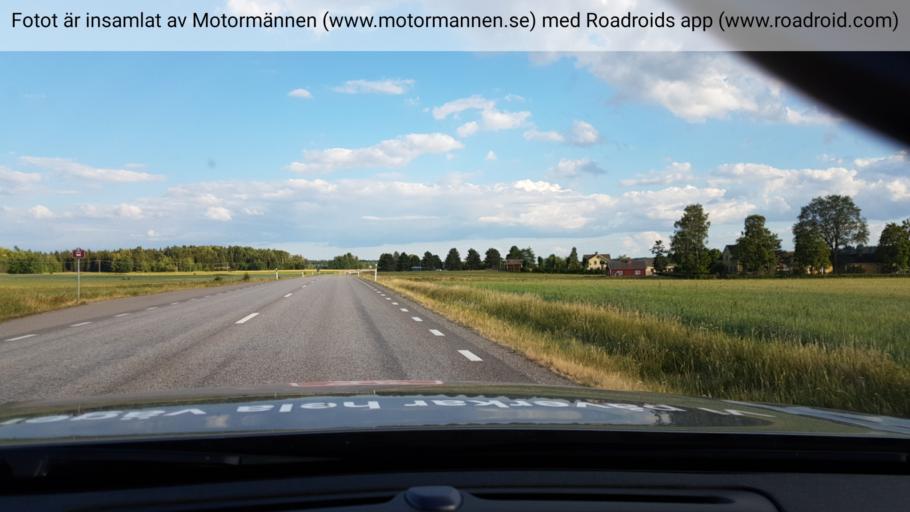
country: SE
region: Uppsala
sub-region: Heby Kommun
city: Heby
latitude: 59.9306
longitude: 16.8734
